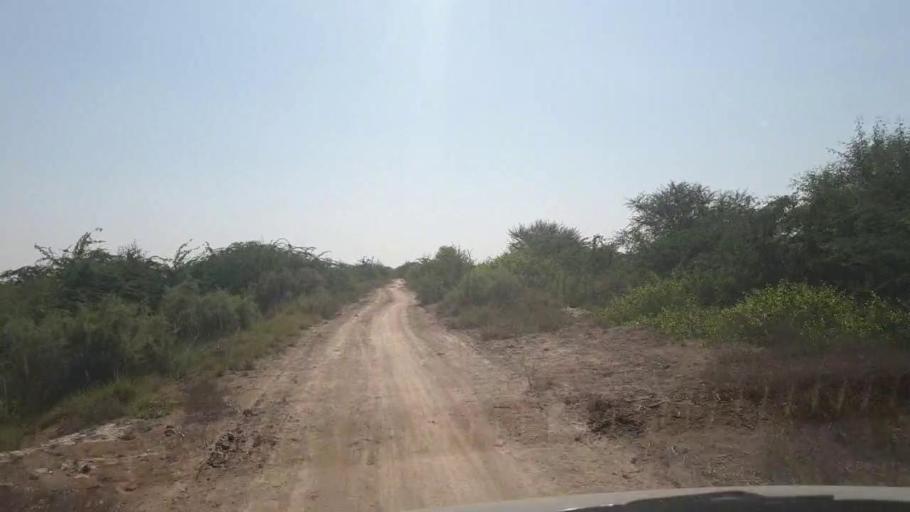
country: PK
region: Sindh
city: Tando Bago
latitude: 24.9106
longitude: 69.1645
